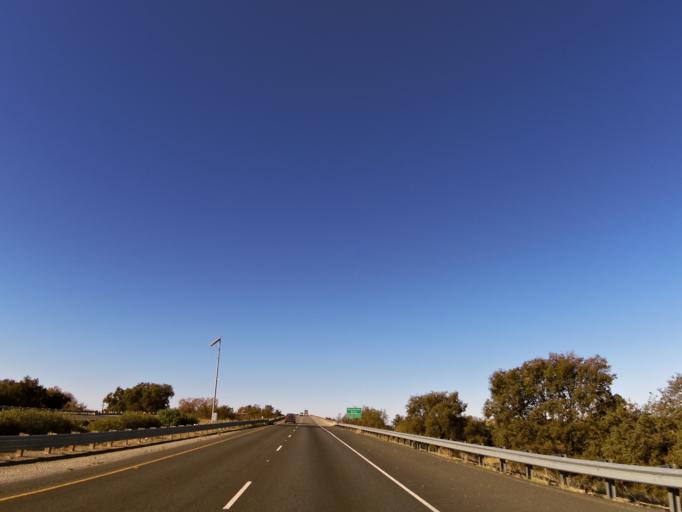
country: US
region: California
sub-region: Yolo County
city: West Sacramento
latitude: 38.6734
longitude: -121.6190
